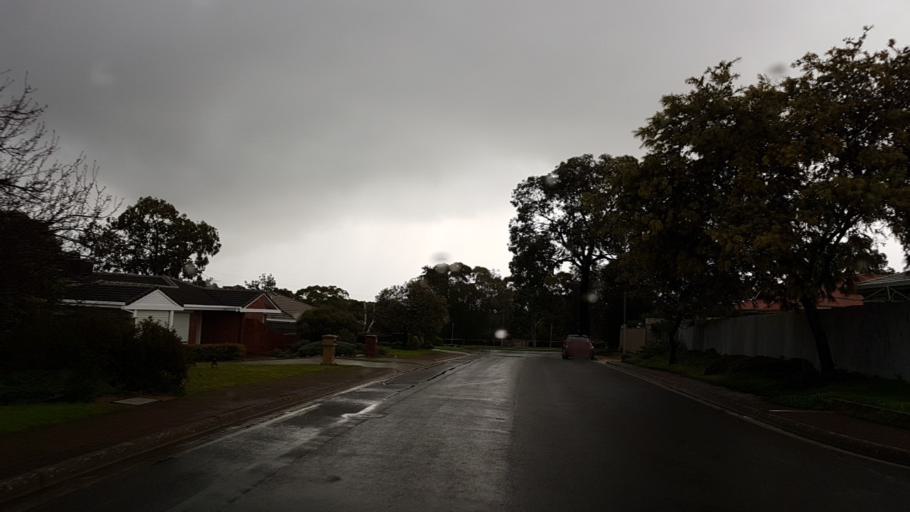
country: AU
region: South Australia
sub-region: Onkaparinga
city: Craigburn Farm
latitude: -35.0853
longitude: 138.5879
